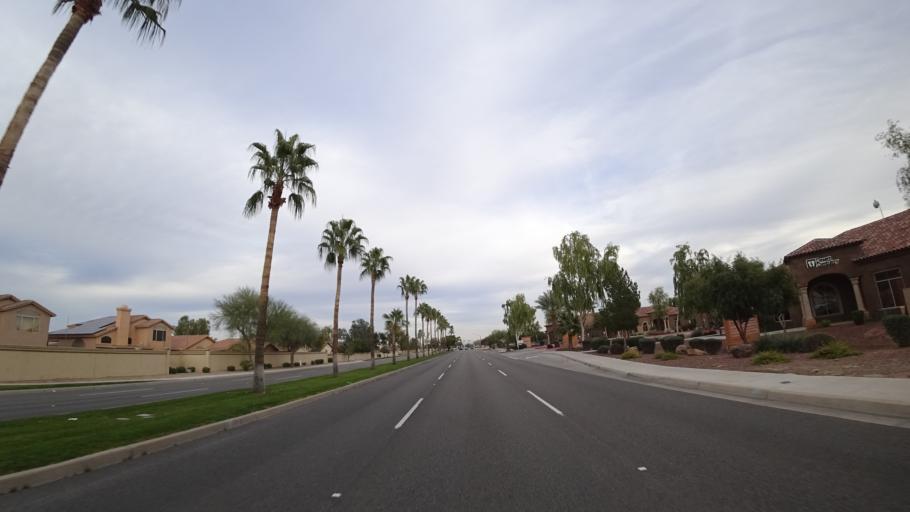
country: US
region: Arizona
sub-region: Maricopa County
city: Sun City West
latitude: 33.6386
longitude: -112.3841
